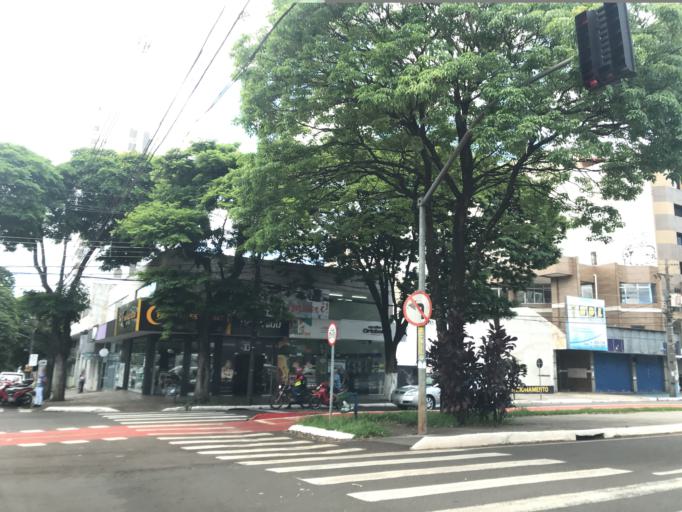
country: BR
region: Parana
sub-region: Maringa
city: Maringa
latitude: -23.4208
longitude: -51.9309
